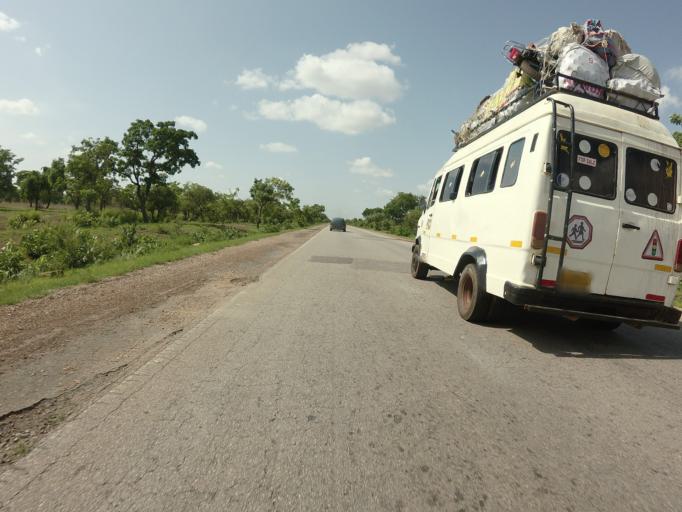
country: GH
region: Northern
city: Savelugu
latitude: 9.9467
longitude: -0.8383
